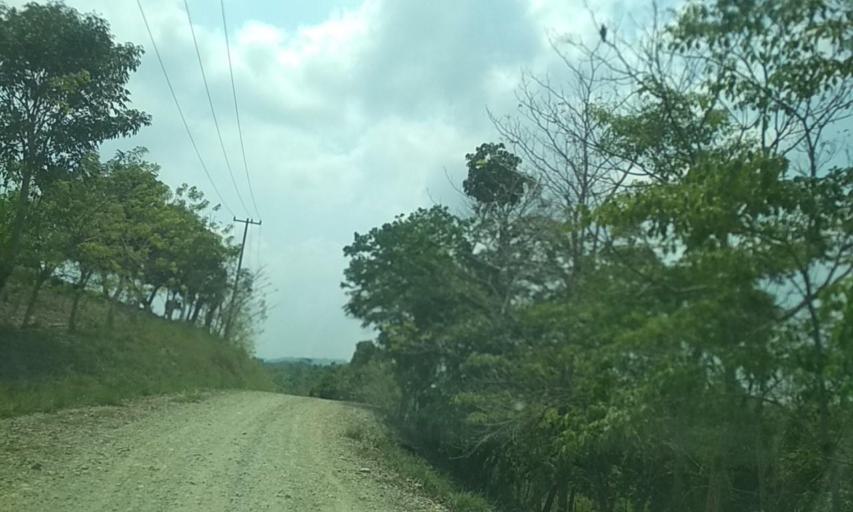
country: MX
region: Tabasco
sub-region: Huimanguillo
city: Francisco Rueda
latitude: 17.6253
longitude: -93.8182
